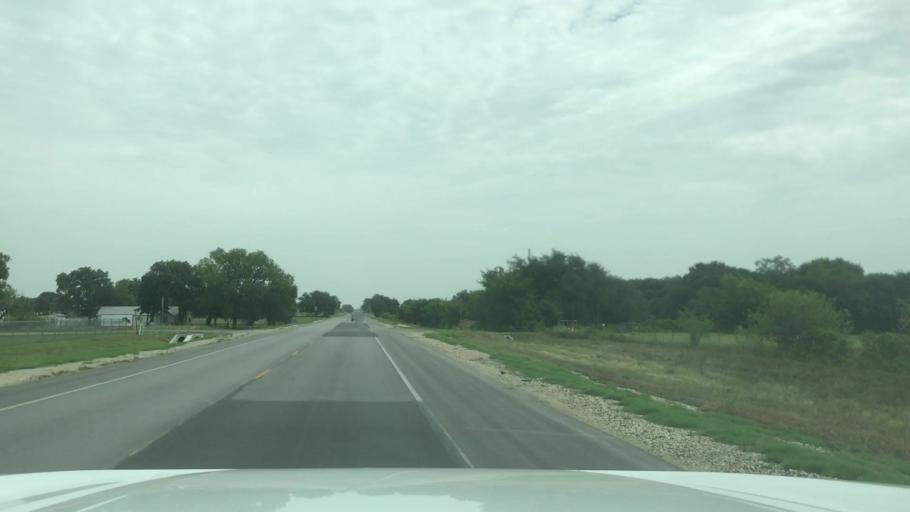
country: US
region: Texas
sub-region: Erath County
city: Dublin
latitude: 32.0892
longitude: -98.2913
